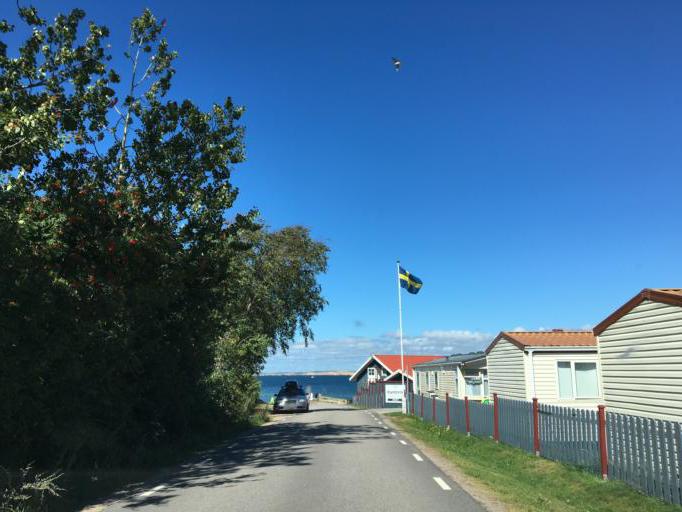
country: SE
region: Vaestra Goetaland
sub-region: Sotenas Kommun
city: Hunnebostrand
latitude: 58.4389
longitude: 11.2671
